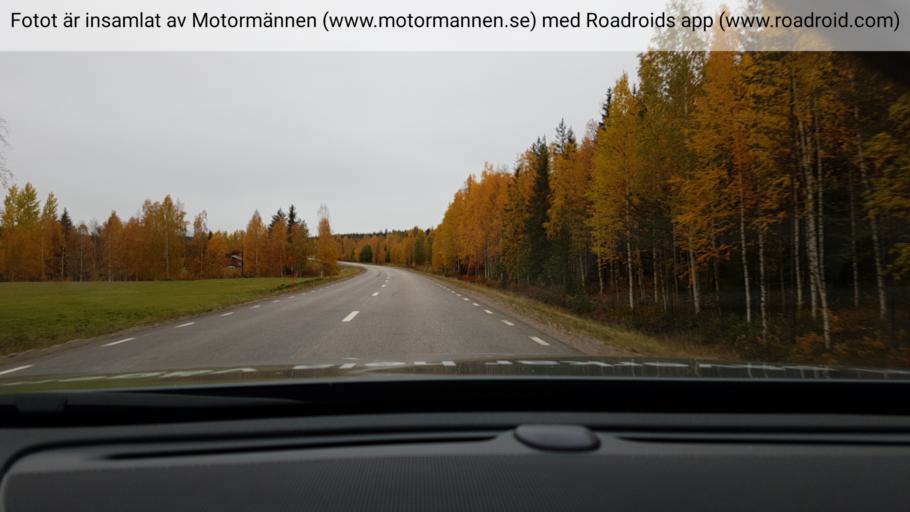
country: SE
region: Norrbotten
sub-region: Overkalix Kommun
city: OEverkalix
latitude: 66.5642
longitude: 22.7614
